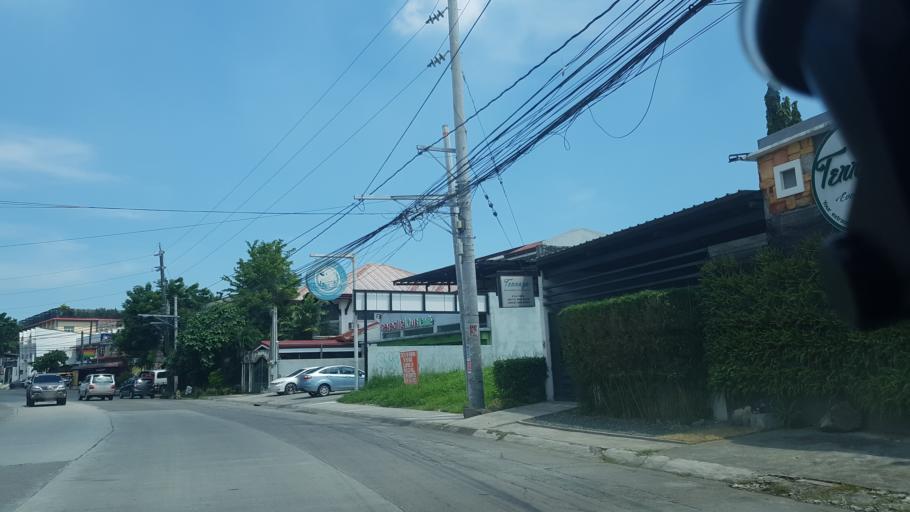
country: PH
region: Calabarzon
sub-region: Province of Rizal
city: Las Pinas
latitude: 14.4324
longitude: 120.9900
